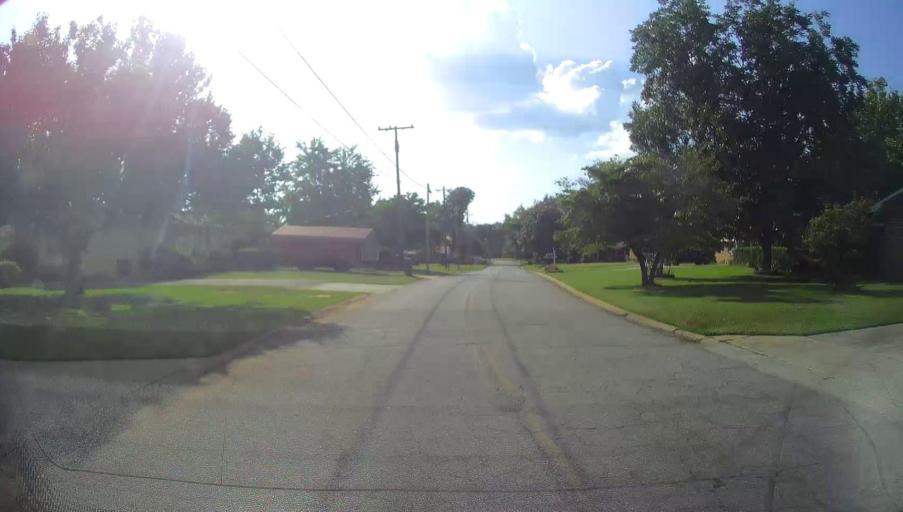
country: US
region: Georgia
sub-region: Houston County
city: Warner Robins
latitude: 32.5986
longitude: -83.6393
